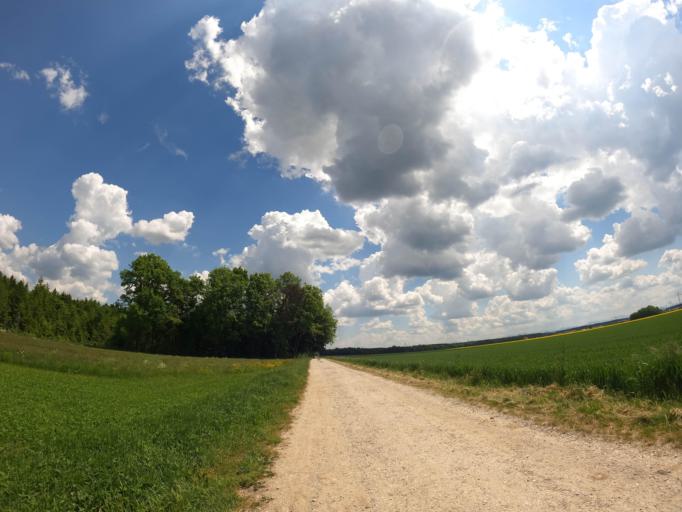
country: DE
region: Bavaria
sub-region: Upper Bavaria
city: Sauerlach
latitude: 47.9861
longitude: 11.6596
